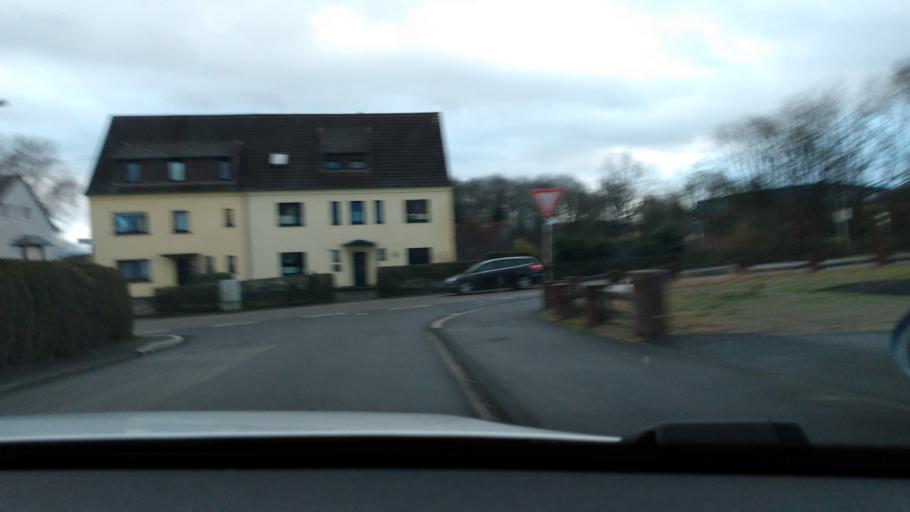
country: DE
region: Rheinland-Pfalz
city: Vettelschoss
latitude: 50.6145
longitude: 7.3142
